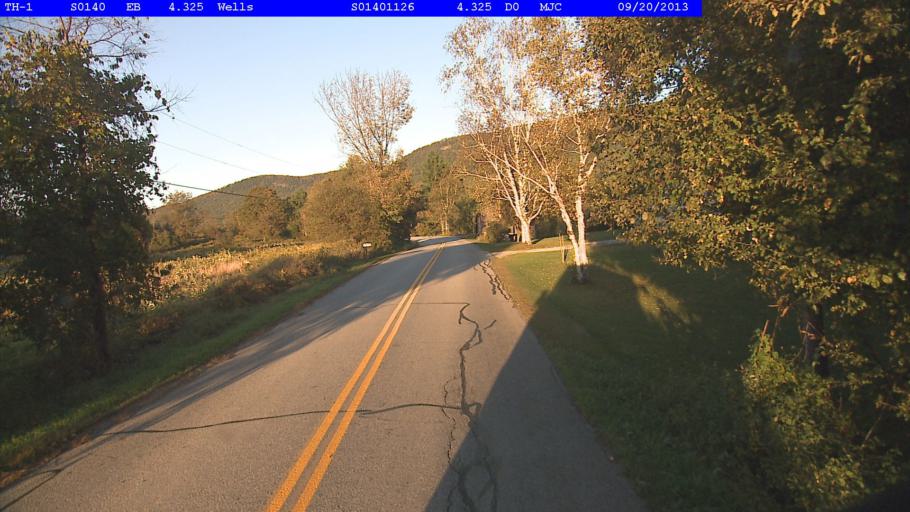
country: US
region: New York
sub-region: Washington County
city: Granville
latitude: 43.4161
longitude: -73.1245
